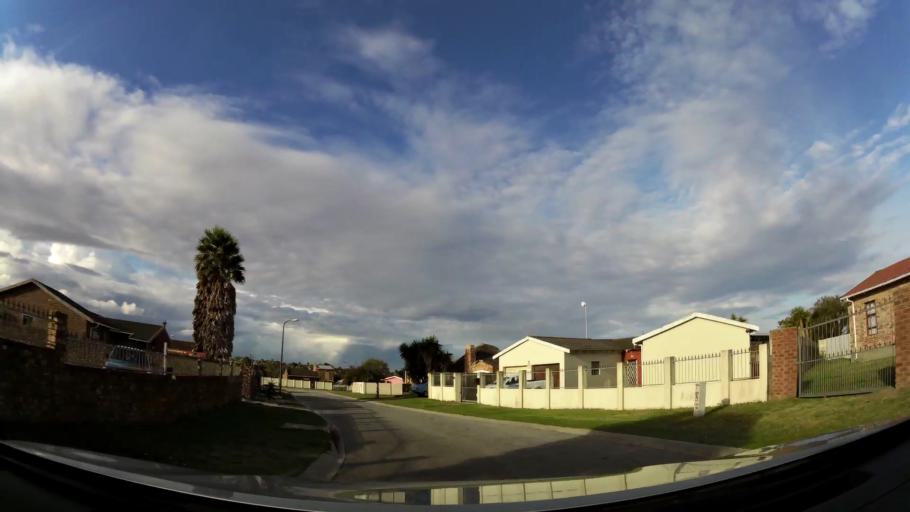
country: ZA
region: Eastern Cape
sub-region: Nelson Mandela Bay Metropolitan Municipality
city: Port Elizabeth
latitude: -33.9650
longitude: 25.4758
